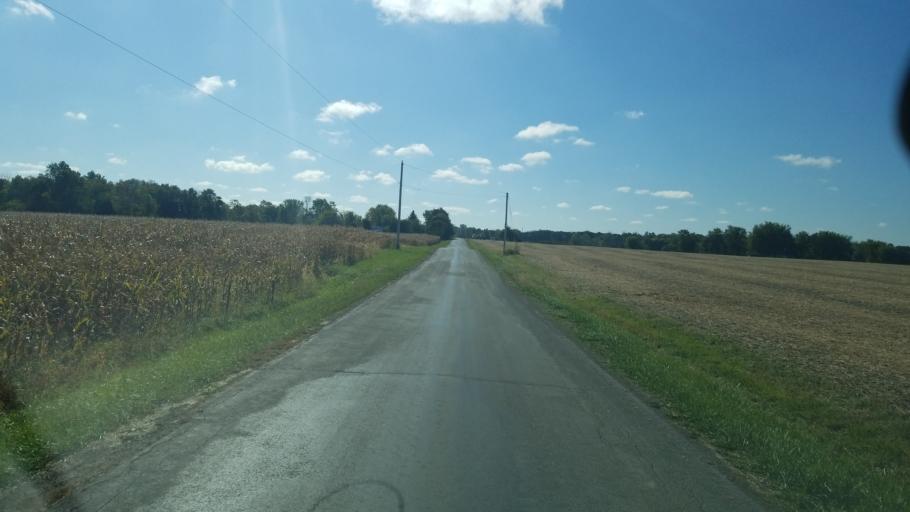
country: US
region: Ohio
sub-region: Highland County
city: Leesburg
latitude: 39.2743
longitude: -83.5538
